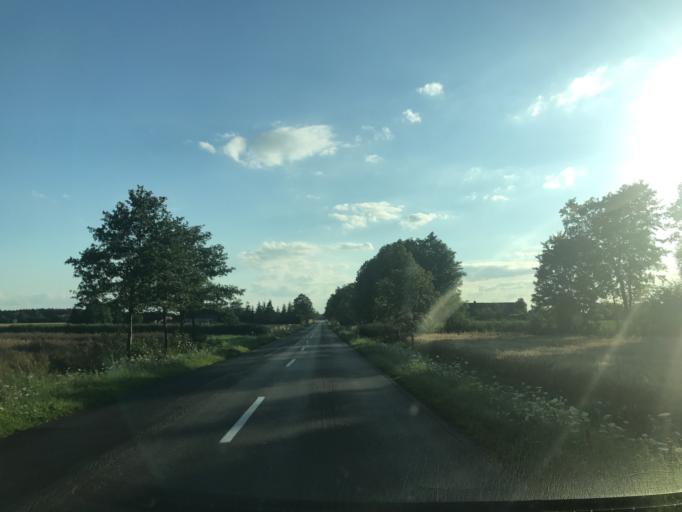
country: PL
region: Greater Poland Voivodeship
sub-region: Powiat pleszewski
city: Czermin
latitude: 52.0036
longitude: 17.6854
